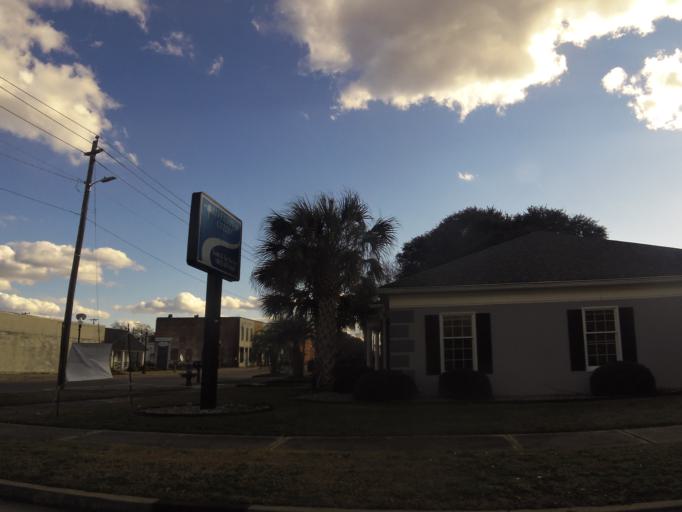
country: US
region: South Carolina
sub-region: Clarendon County
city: Manning
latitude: 33.6966
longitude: -80.2121
